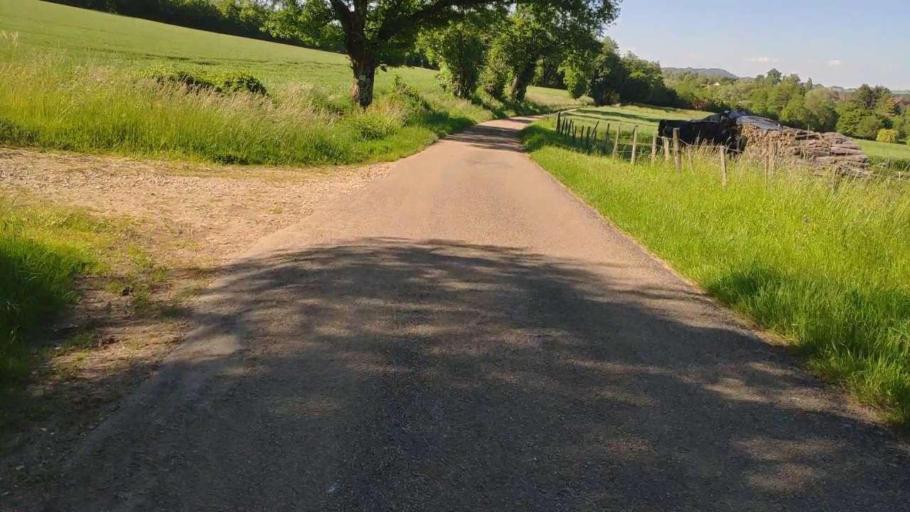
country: FR
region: Franche-Comte
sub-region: Departement du Jura
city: Montmorot
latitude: 46.7252
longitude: 5.5516
